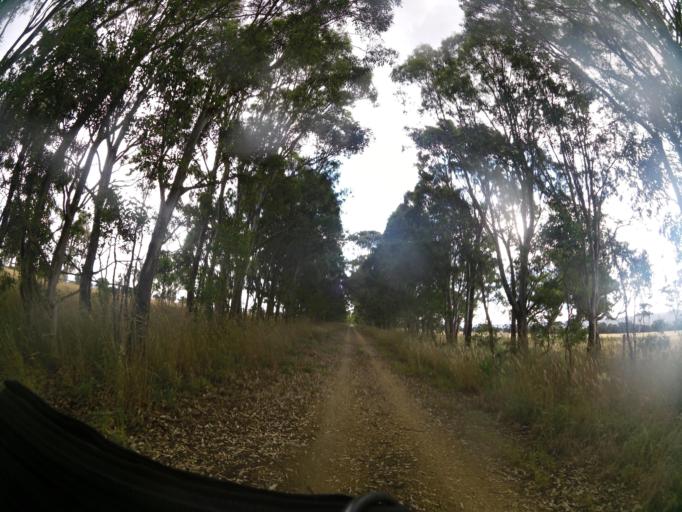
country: AU
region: Victoria
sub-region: Wellington
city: Heyfield
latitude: -38.0290
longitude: 146.6652
